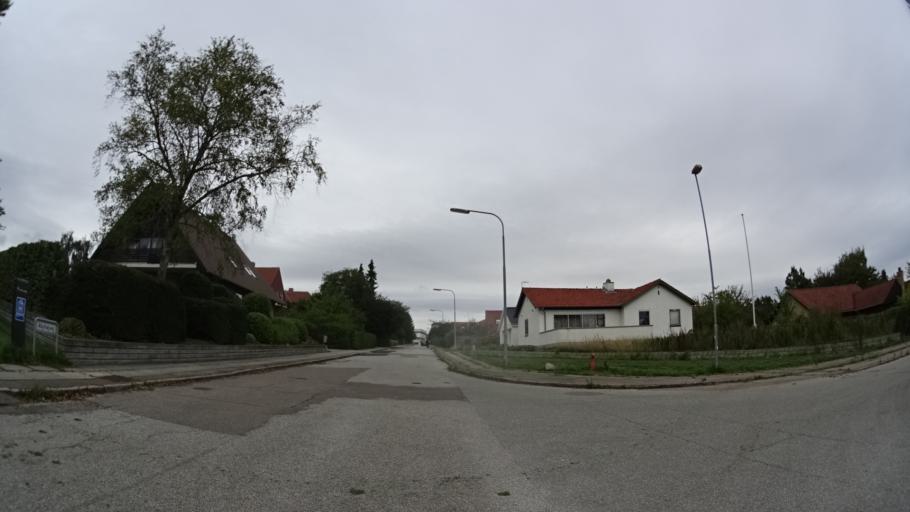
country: DK
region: Central Jutland
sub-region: Arhus Kommune
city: Arhus
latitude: 56.1637
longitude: 10.1619
